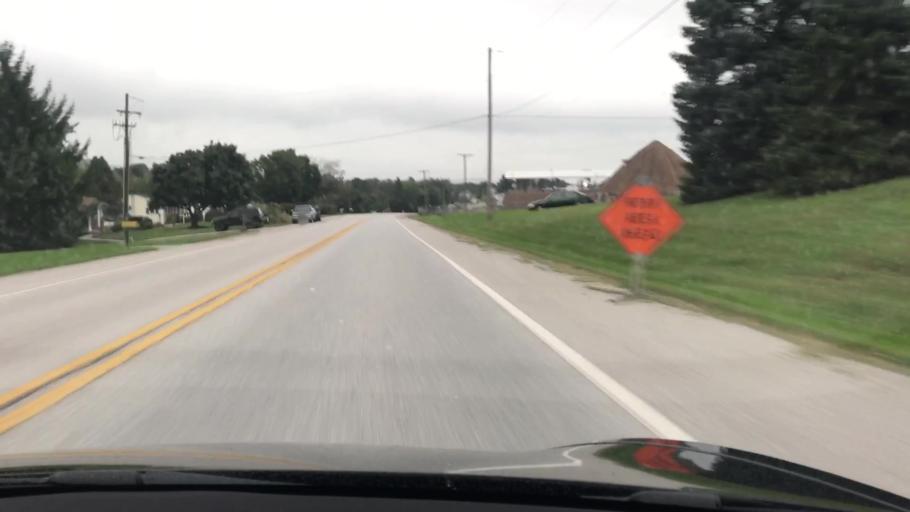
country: US
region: Pennsylvania
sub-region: York County
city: Dover
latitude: 39.9944
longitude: -76.8565
